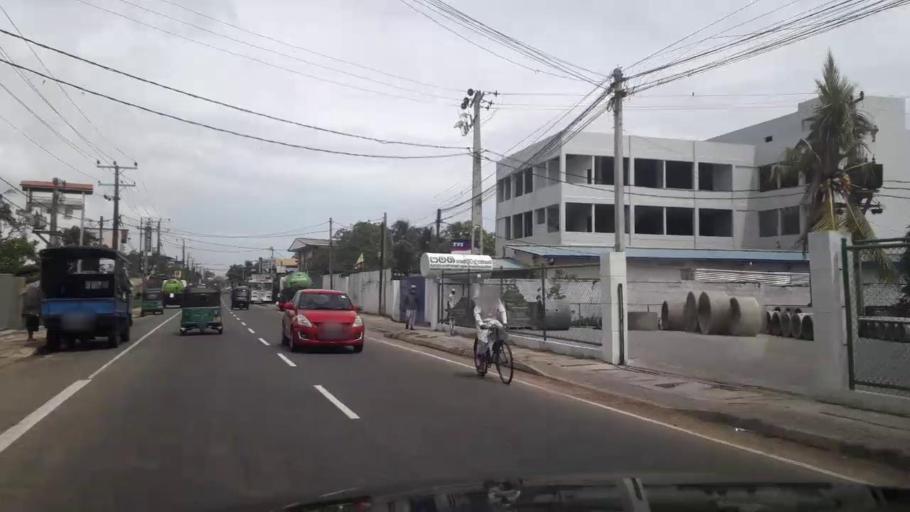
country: LK
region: Western
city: Panadura
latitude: 6.7460
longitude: 79.9016
